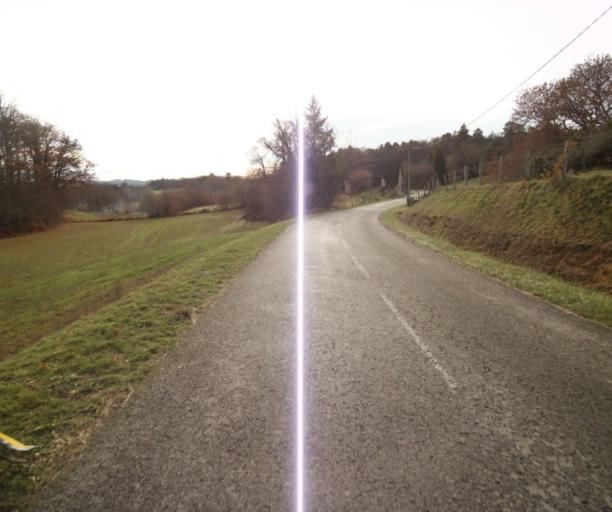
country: FR
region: Limousin
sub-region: Departement de la Correze
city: Chameyrat
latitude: 45.2466
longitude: 1.6988
